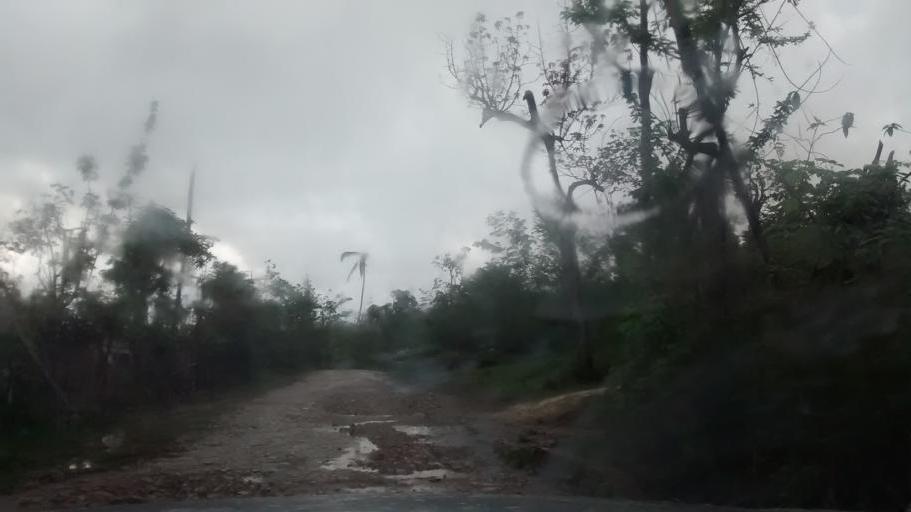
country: HT
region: Grandans
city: Corail
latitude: 18.5321
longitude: -73.9517
